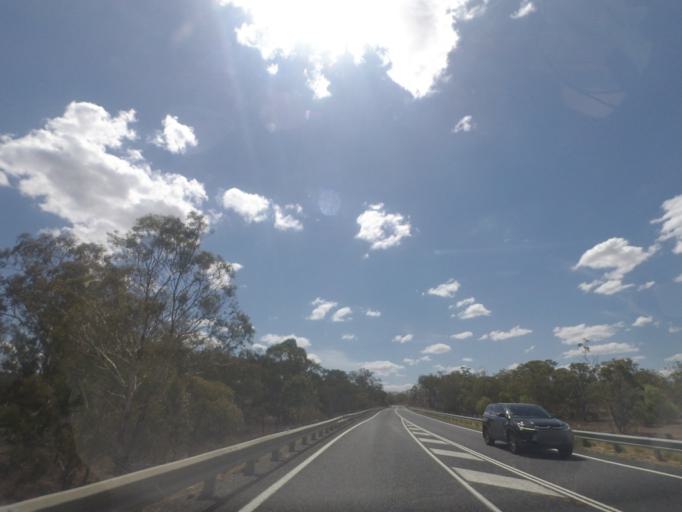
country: AU
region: Queensland
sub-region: Southern Downs
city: Warwick
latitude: -28.1625
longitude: 151.6980
